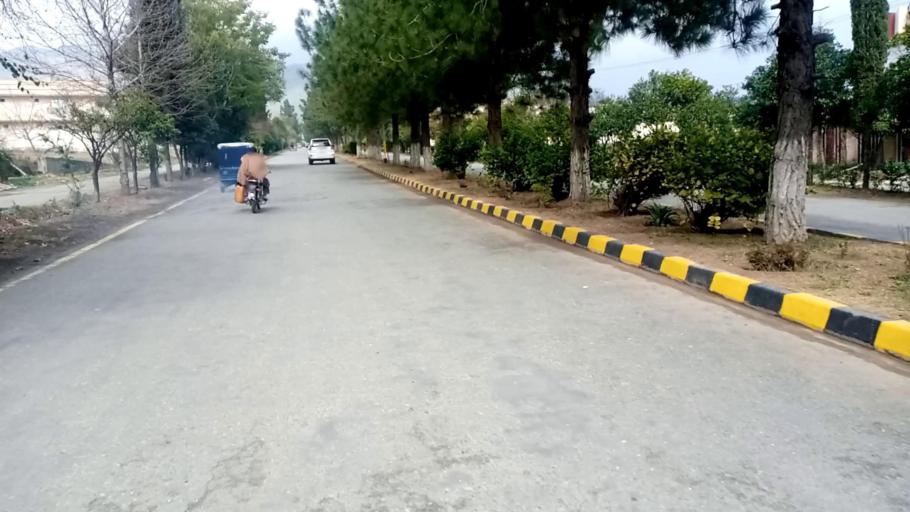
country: PK
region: Khyber Pakhtunkhwa
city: Mingora
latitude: 34.8215
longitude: 72.3406
